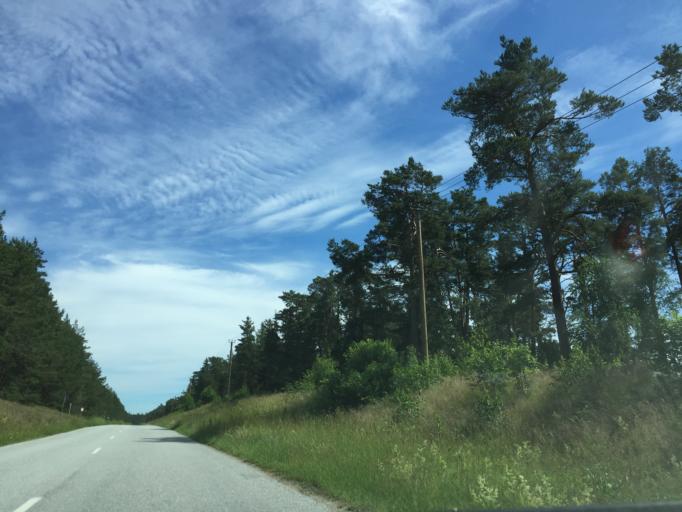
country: LV
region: Rojas
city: Roja
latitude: 57.5753
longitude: 22.6298
